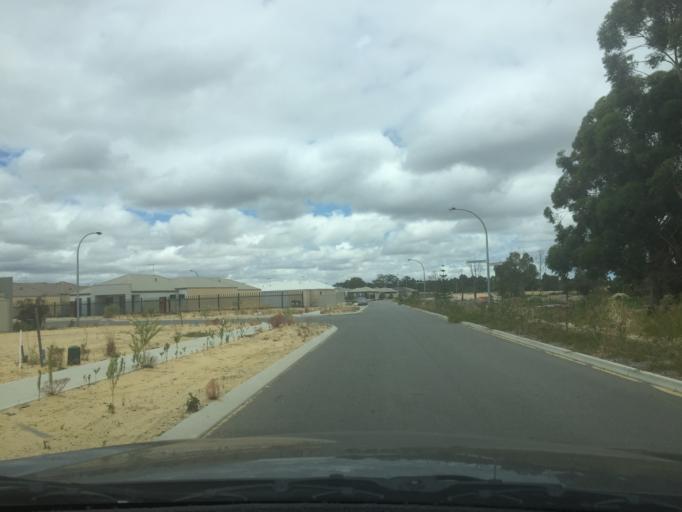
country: AU
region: Western Australia
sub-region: Armadale
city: Harrisdale
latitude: -32.1362
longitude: 115.9063
